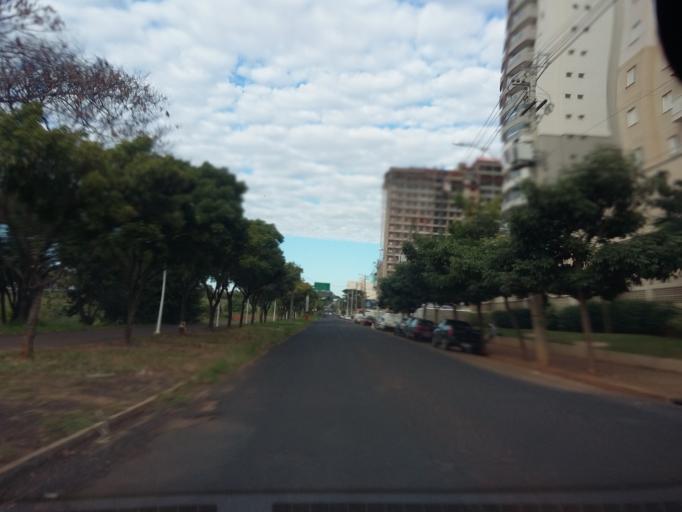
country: BR
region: Sao Paulo
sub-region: Sao Jose Do Rio Preto
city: Sao Jose do Rio Preto
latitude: -20.8368
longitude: -49.4086
